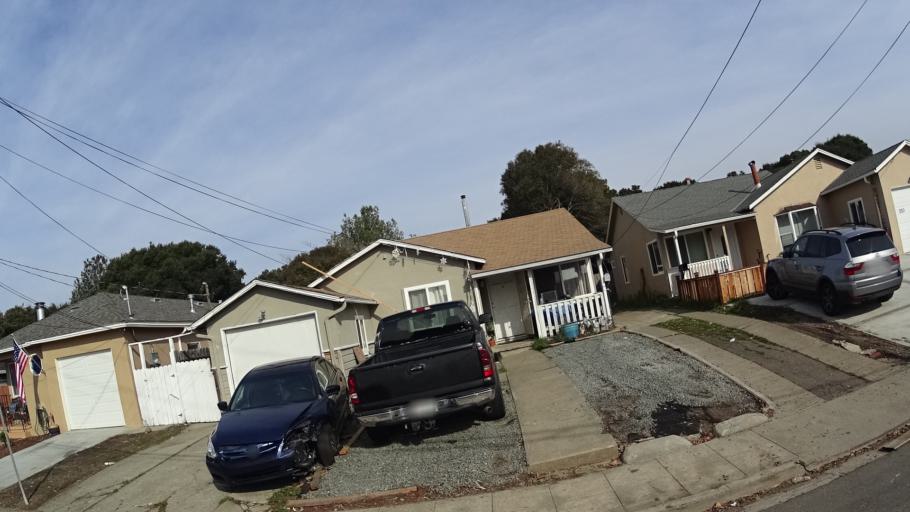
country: US
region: California
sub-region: Alameda County
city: Hayward
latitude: 37.6661
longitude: -122.0682
